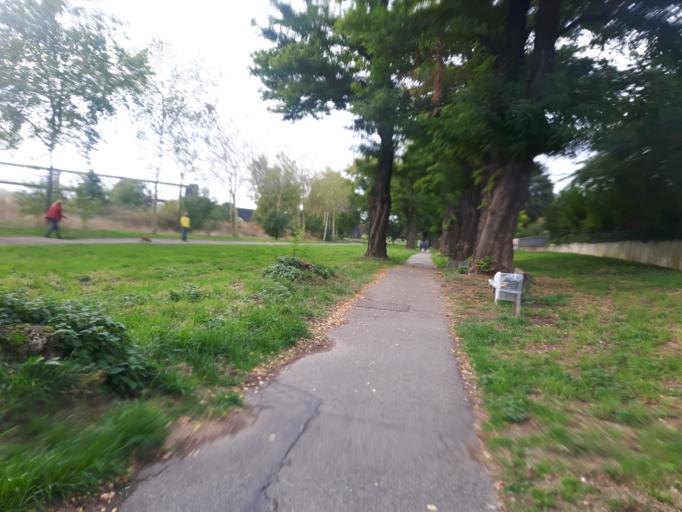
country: DE
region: Rheinland-Pfalz
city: Urmitz
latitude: 50.4240
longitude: 7.5310
